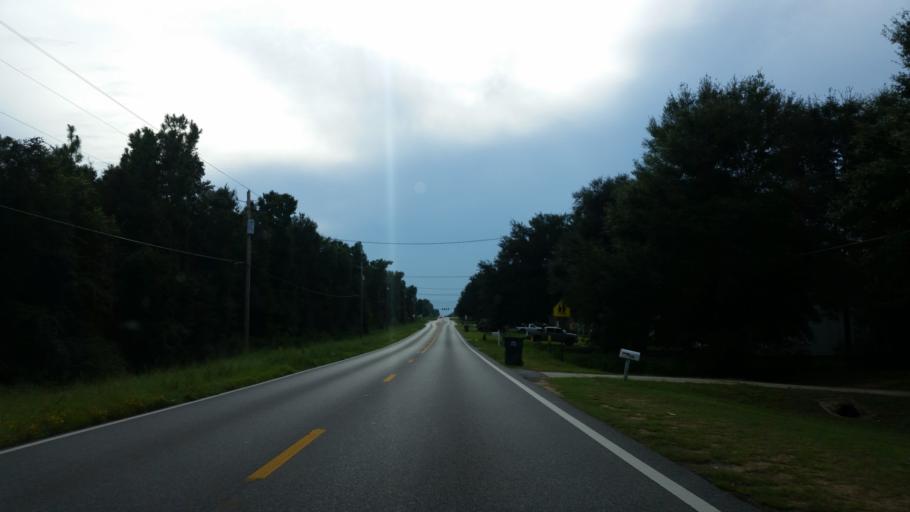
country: US
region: Florida
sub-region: Santa Rosa County
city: Bagdad
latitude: 30.5739
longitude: -87.0920
